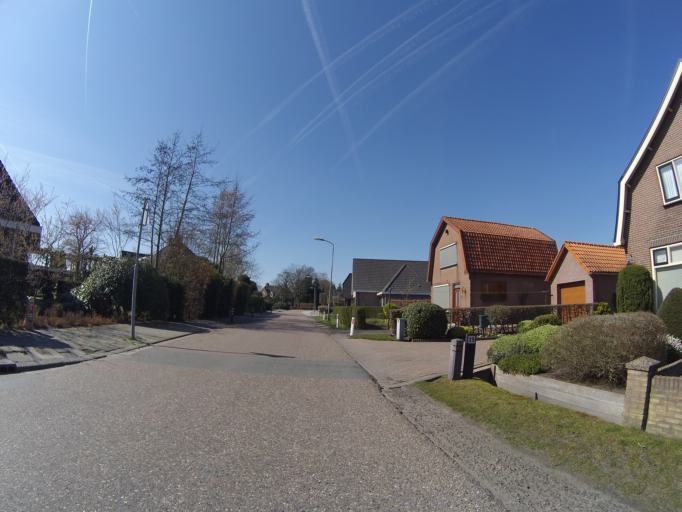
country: NL
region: Gelderland
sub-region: Gemeente Nijkerk
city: Nijkerk
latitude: 52.1999
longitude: 5.4541
